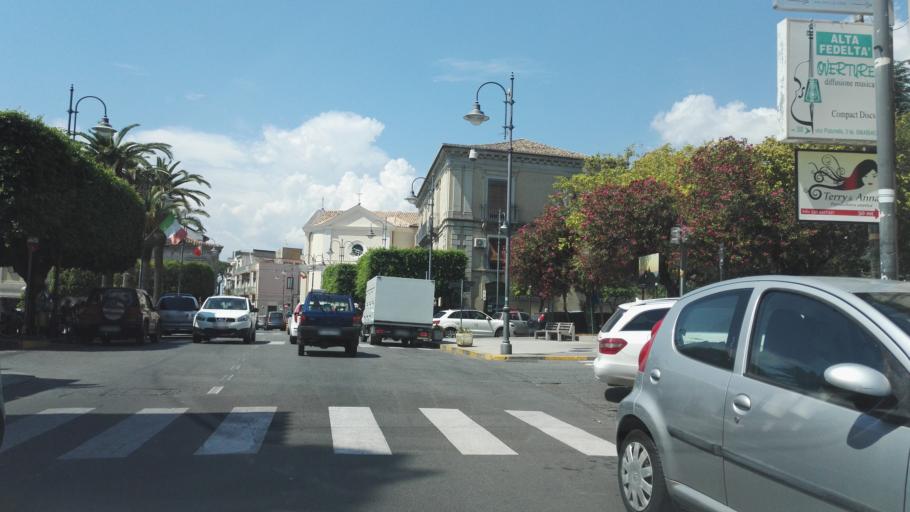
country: IT
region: Calabria
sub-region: Provincia di Reggio Calabria
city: Roccella Ionica
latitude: 38.3221
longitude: 16.4054
